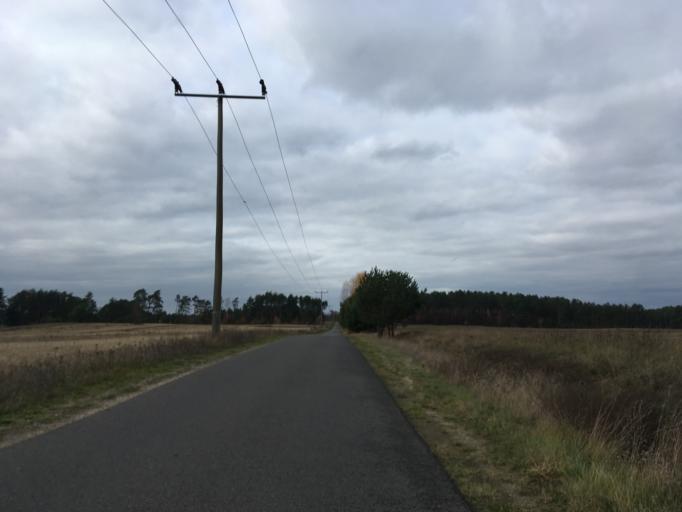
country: DE
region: Brandenburg
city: Jamlitz
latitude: 52.0822
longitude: 14.4485
